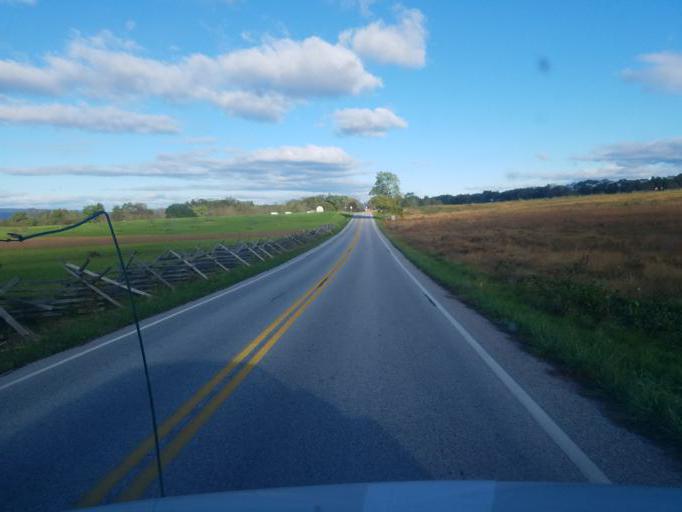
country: US
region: Pennsylvania
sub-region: Adams County
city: Gettysburg
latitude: 39.8458
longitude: -77.2433
